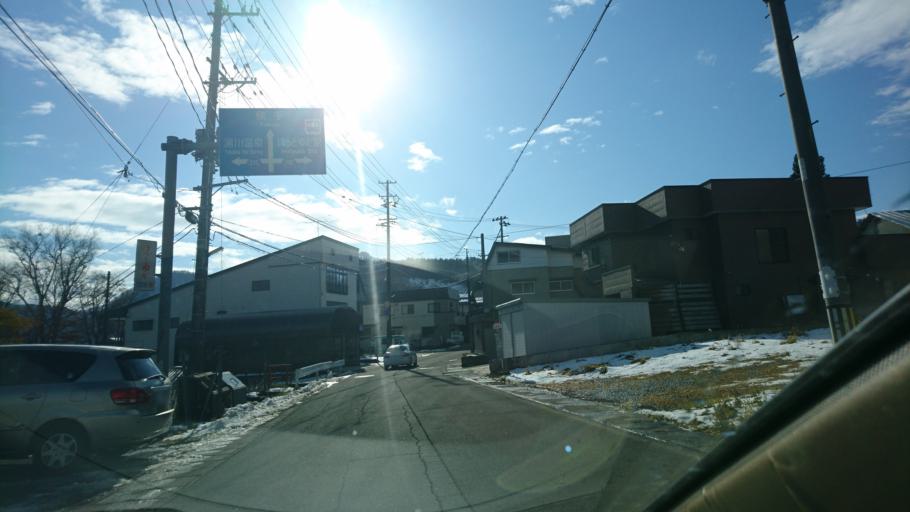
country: JP
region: Akita
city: Yokotemachi
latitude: 39.3154
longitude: 140.7778
